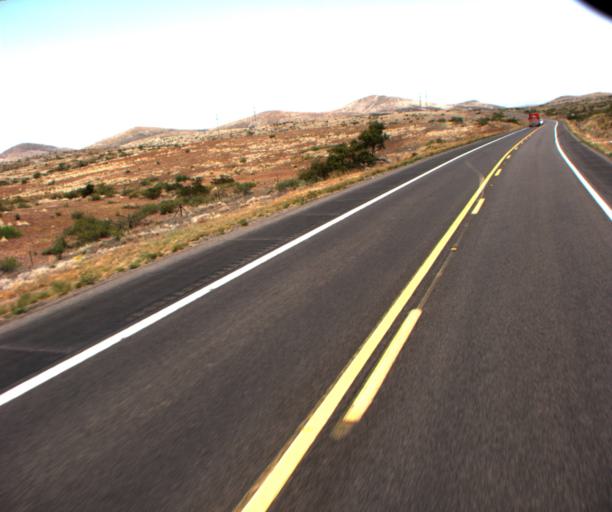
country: US
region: Arizona
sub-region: Greenlee County
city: Clifton
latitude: 32.7489
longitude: -109.2300
